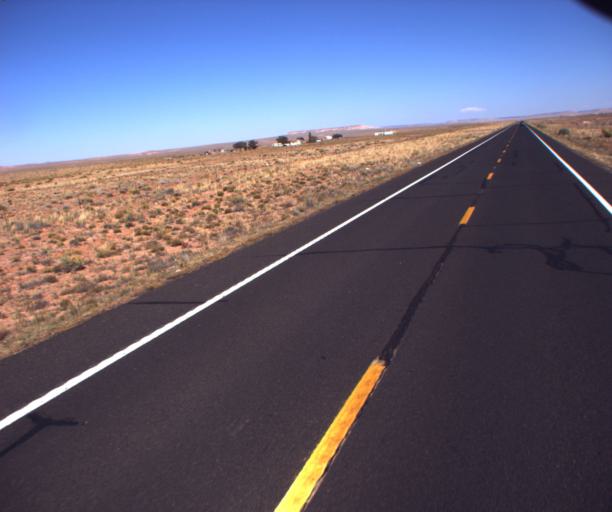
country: US
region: Arizona
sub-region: Coconino County
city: Tuba City
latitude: 36.1512
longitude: -111.1322
